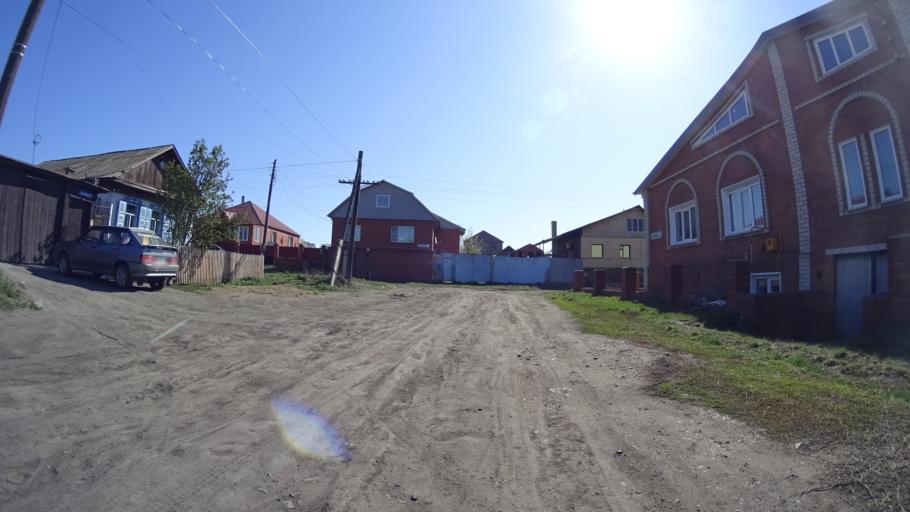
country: RU
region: Chelyabinsk
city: Troitsk
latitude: 54.0974
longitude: 61.5964
